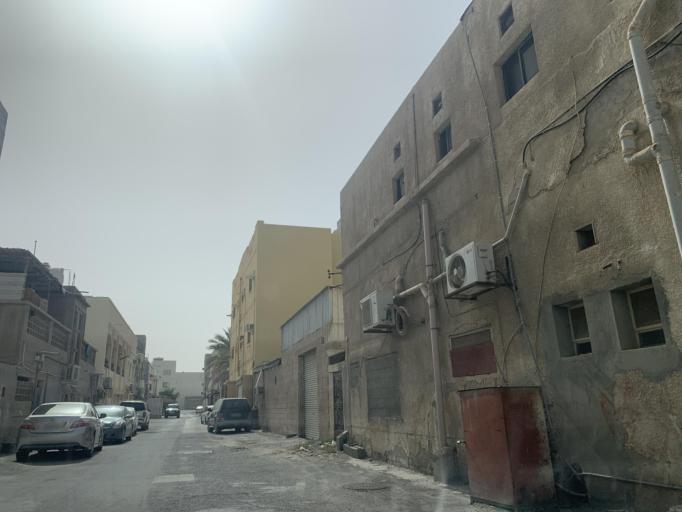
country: BH
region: Northern
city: Madinat `Isa
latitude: 26.1566
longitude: 50.5184
